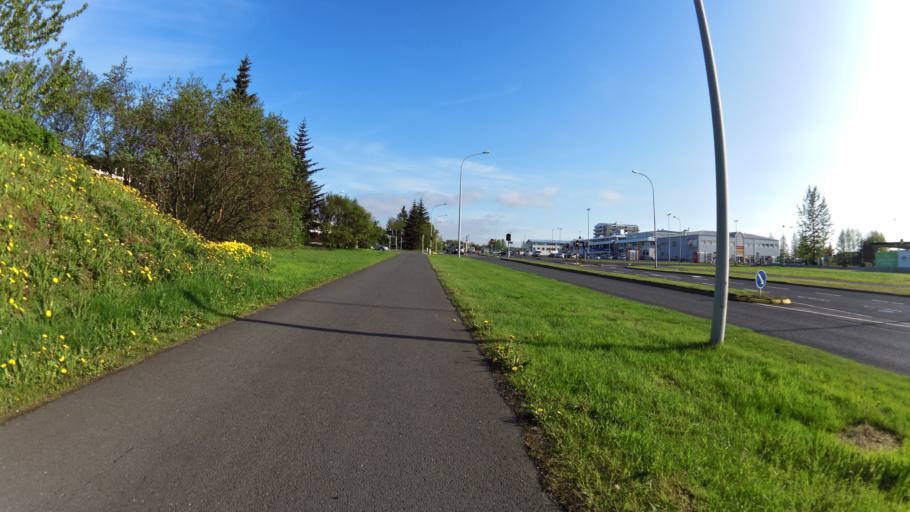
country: IS
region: Capital Region
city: Reykjavik
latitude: 64.1106
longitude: -21.8405
